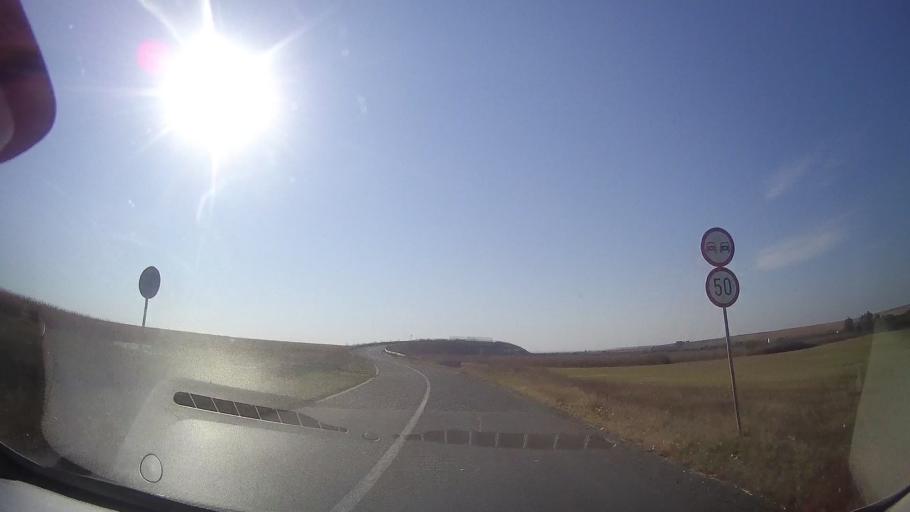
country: RO
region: Timis
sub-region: Comuna Topolovatu Mare
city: Topolovatu Mare
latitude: 45.8081
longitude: 21.5841
